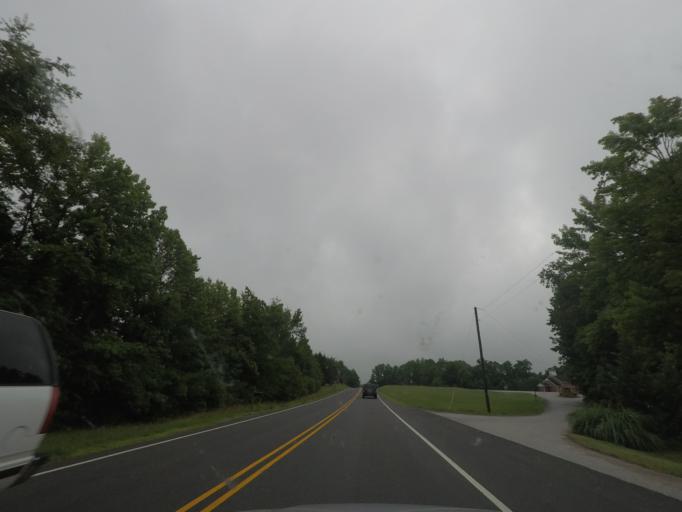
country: US
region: Virginia
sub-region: Prince Edward County
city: Hampden Sydney
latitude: 37.1254
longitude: -78.4513
